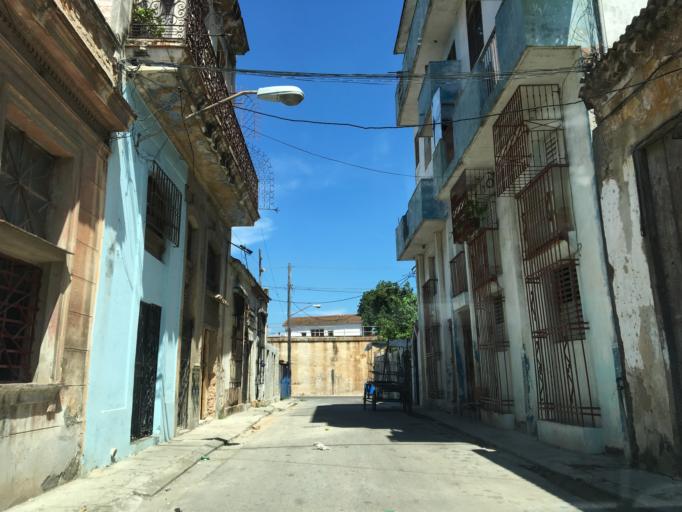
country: CU
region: La Habana
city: La Habana Vieja
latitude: 23.1273
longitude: -82.3574
